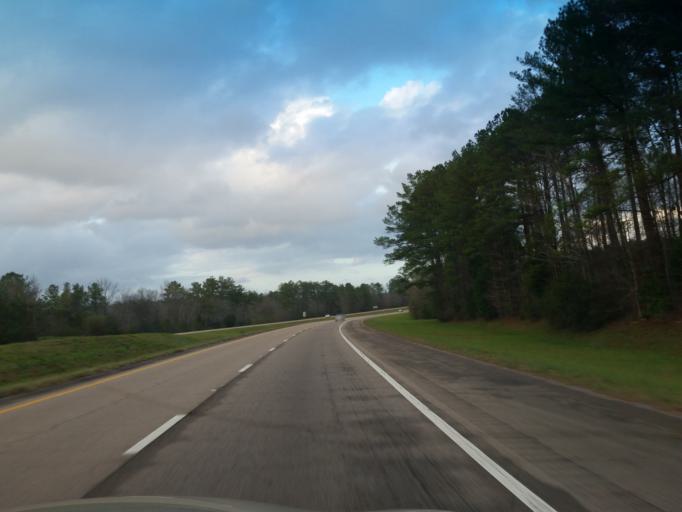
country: US
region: Mississippi
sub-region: Clarke County
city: Stonewall
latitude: 32.0441
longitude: -88.9197
